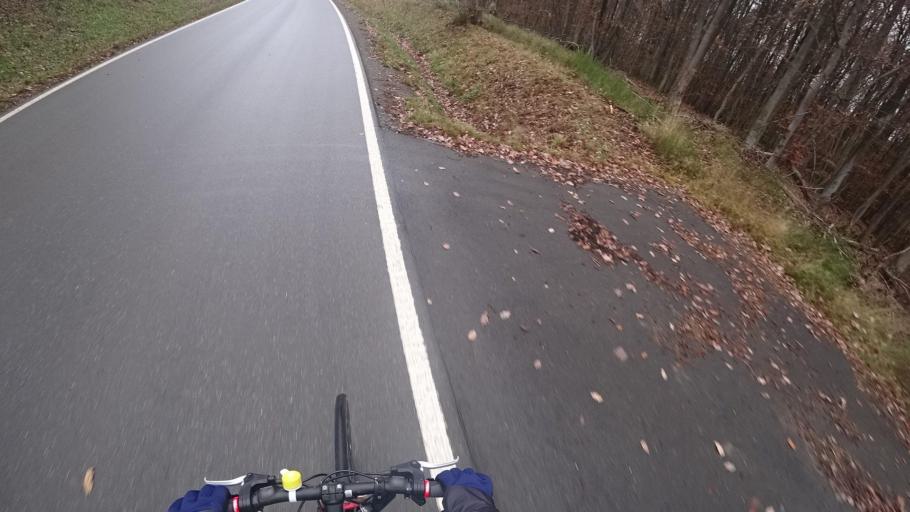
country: DE
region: Rheinland-Pfalz
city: Kratzenburg
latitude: 50.1831
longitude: 7.5483
